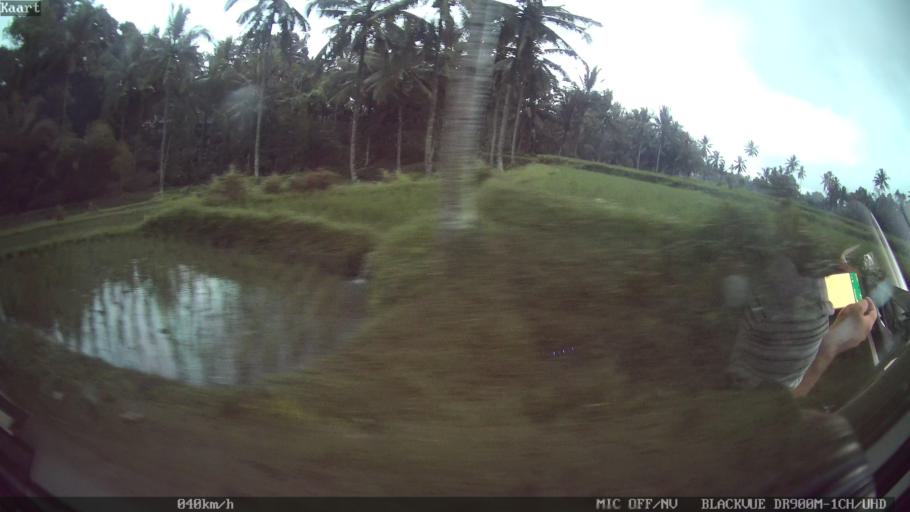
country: ID
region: Bali
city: Kekeran
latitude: -8.4793
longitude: 115.1853
